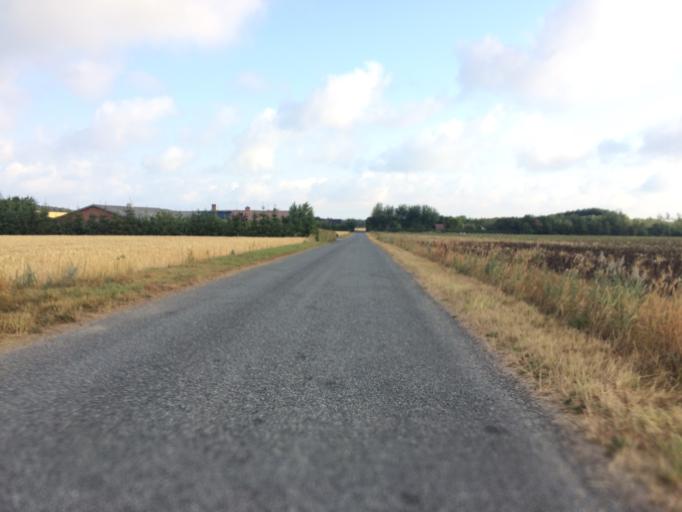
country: DK
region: Central Jutland
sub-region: Holstebro Kommune
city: Vinderup
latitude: 56.6064
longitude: 8.7193
